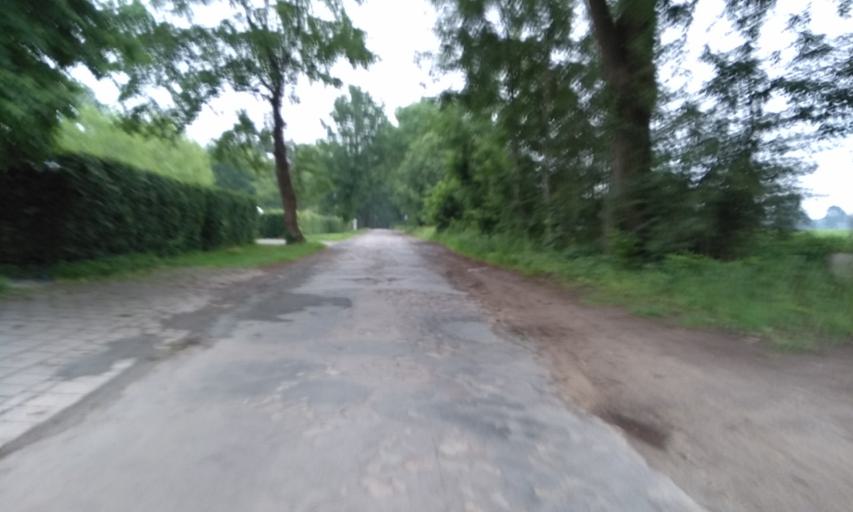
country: DE
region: Lower Saxony
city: Deinste
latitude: 53.5306
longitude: 9.4353
